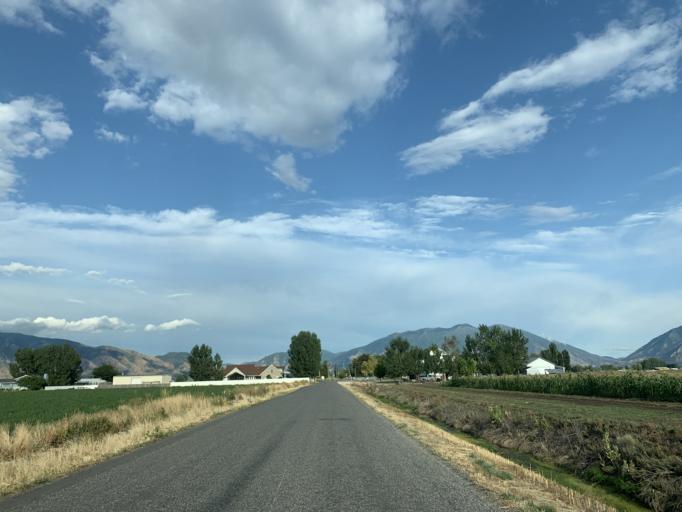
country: US
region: Utah
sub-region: Utah County
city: Benjamin
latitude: 40.1292
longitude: -111.7336
